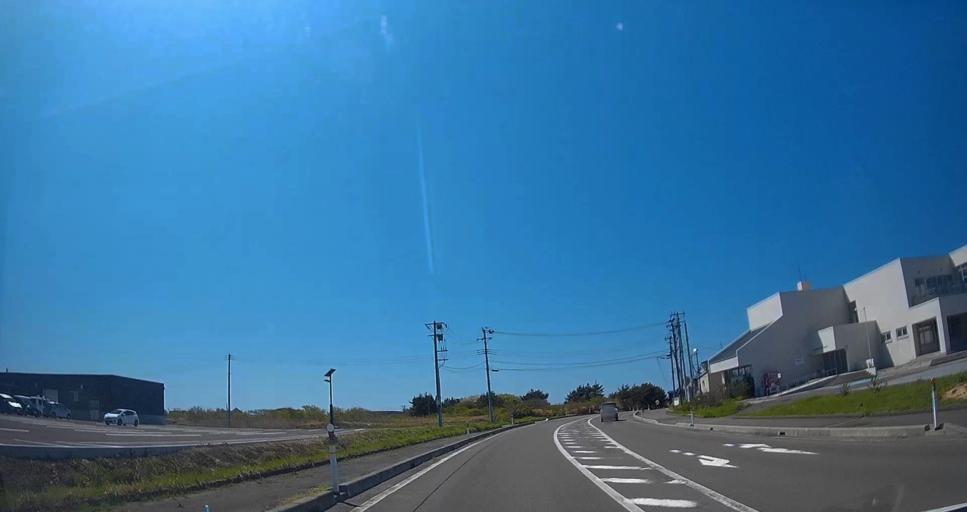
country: JP
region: Hokkaido
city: Hakodate
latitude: 41.5227
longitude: 140.9047
